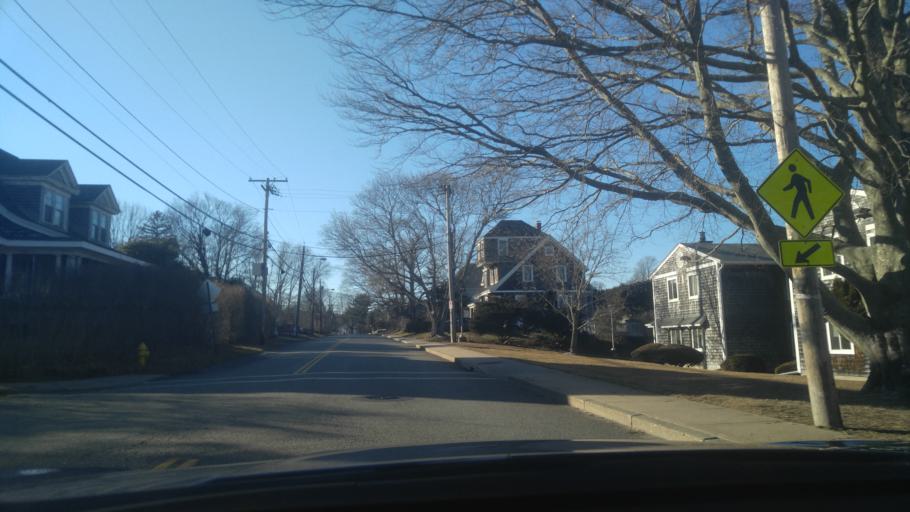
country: US
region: Rhode Island
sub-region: Washington County
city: Narragansett Pier
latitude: 41.4231
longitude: -71.4579
